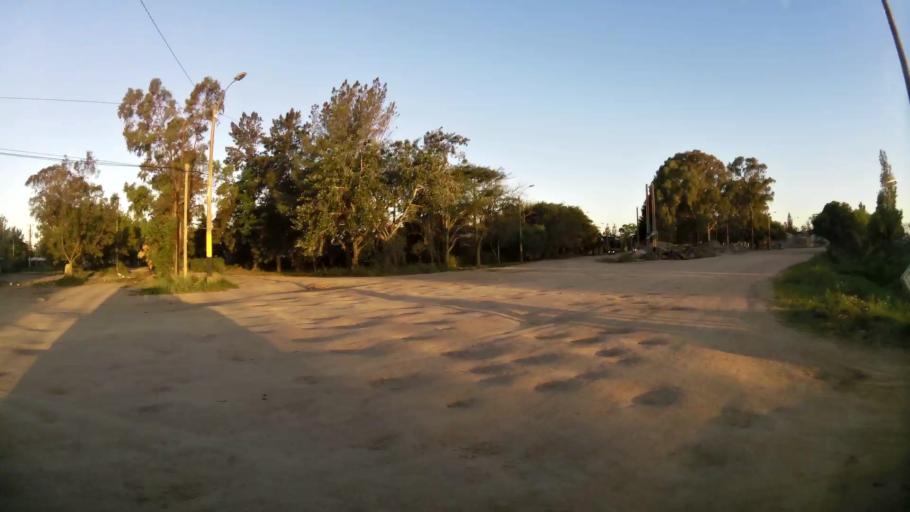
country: UY
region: Canelones
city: Barra de Carrasco
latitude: -34.8408
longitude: -55.9877
